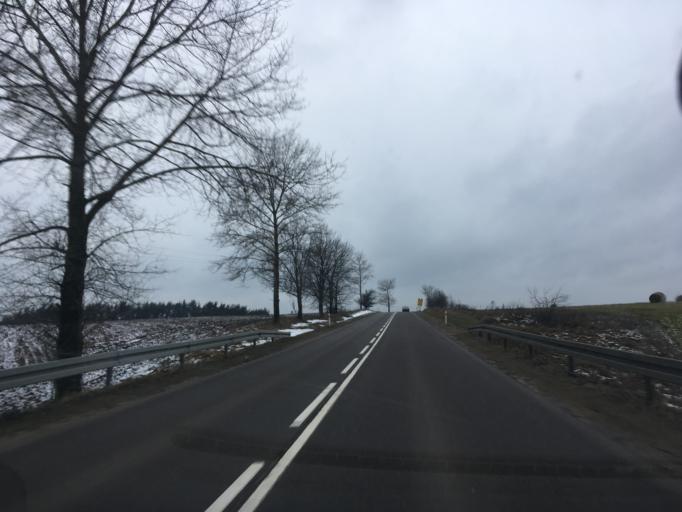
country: PL
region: Podlasie
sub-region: Suwalki
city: Suwalki
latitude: 54.1052
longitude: 22.8880
